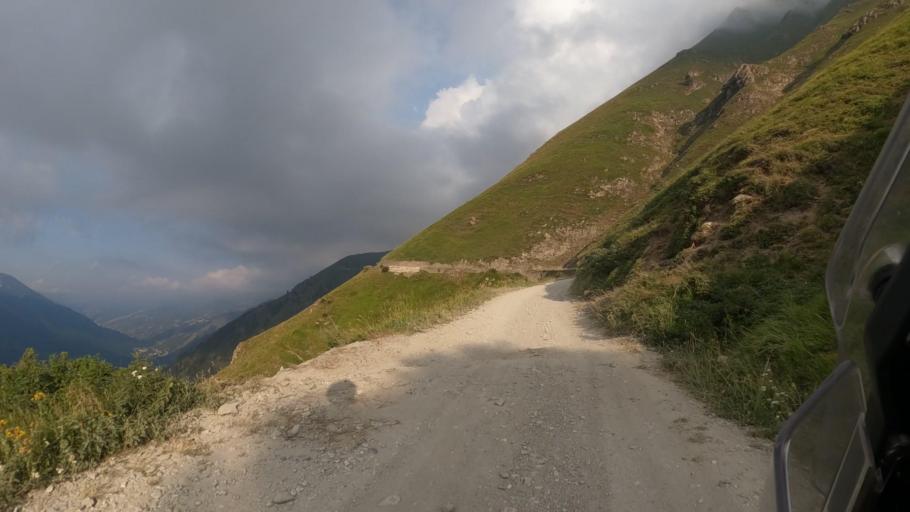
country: IT
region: Piedmont
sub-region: Provincia di Torino
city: Usseaux
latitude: 45.0627
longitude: 7.0223
